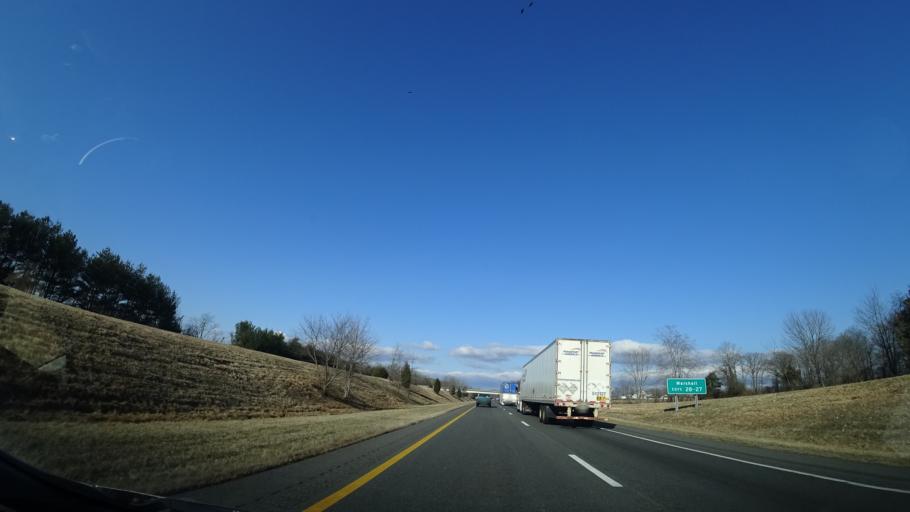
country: US
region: Virginia
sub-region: Fauquier County
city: Marshall
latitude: 38.8577
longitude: -77.8170
